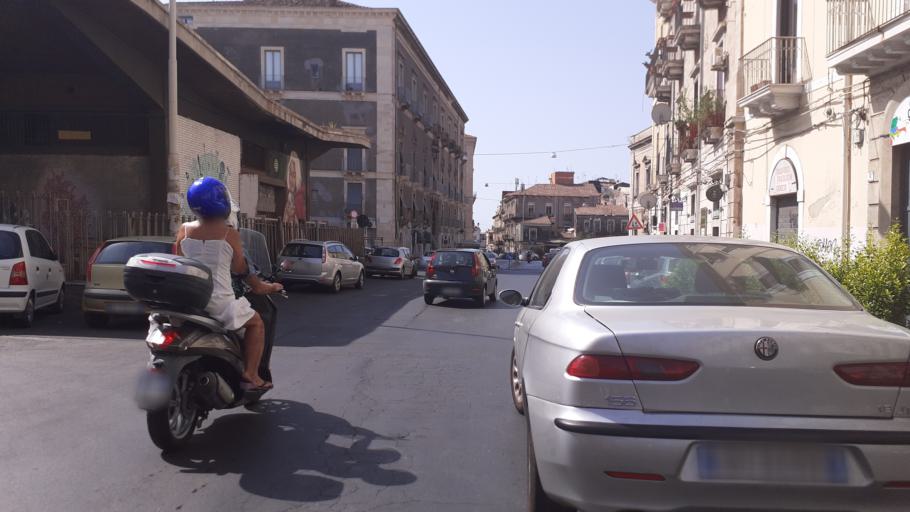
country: IT
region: Sicily
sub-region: Catania
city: Catania
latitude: 37.5045
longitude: 15.0934
